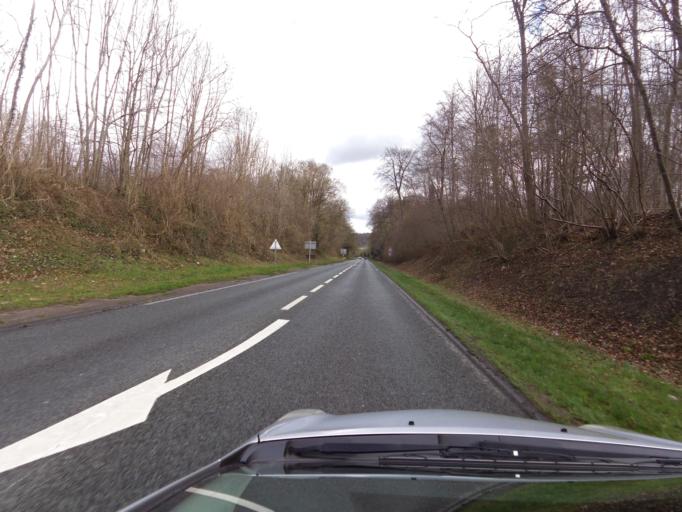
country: FR
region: Picardie
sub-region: Departement de l'Oise
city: Pont-Sainte-Maxence
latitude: 49.2855
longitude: 2.6014
